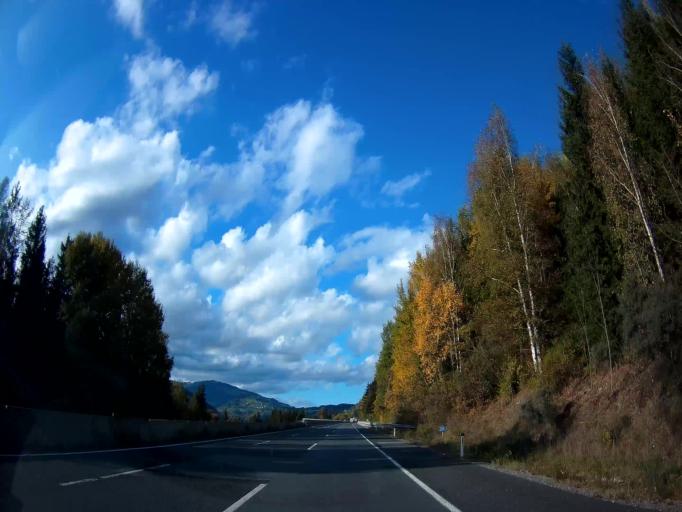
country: AT
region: Carinthia
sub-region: Politischer Bezirk Wolfsberg
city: Wolfsberg
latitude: 46.8718
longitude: 14.8346
